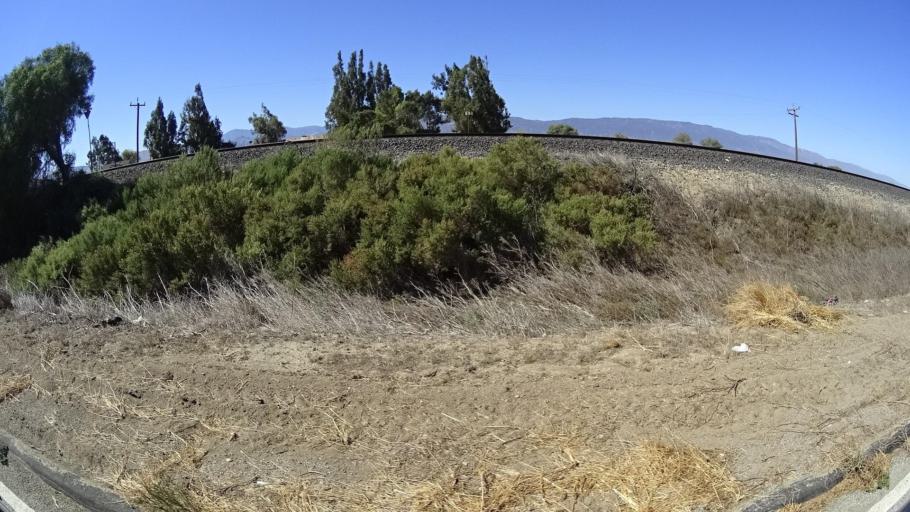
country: US
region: California
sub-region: Monterey County
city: Greenfield
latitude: 36.3653
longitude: -121.2345
